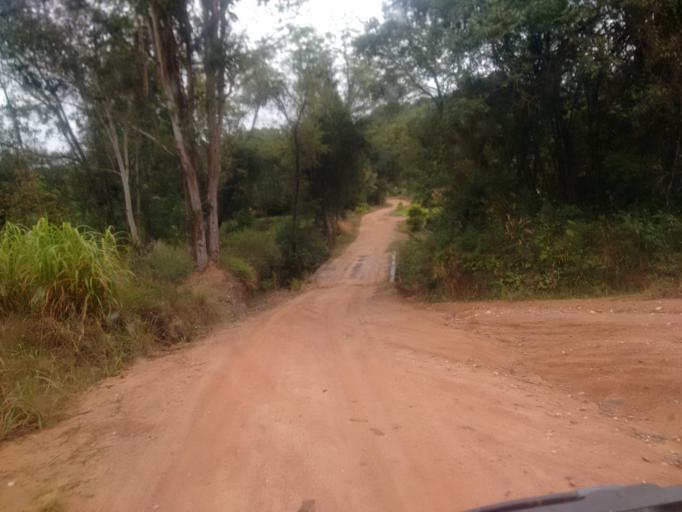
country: BR
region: Rio Grande do Sul
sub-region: Camaqua
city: Camaqua
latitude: -30.7208
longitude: -51.8729
